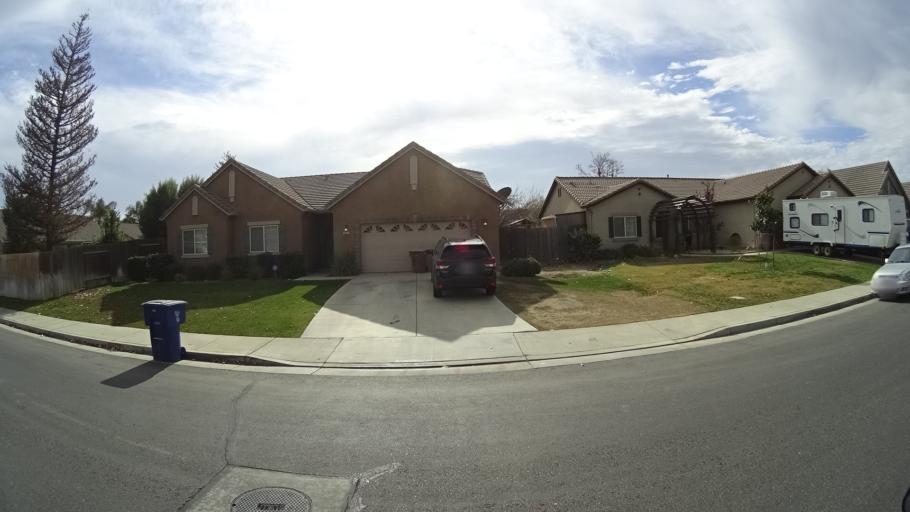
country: US
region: California
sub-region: Kern County
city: Rosedale
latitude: 35.4212
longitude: -119.1408
